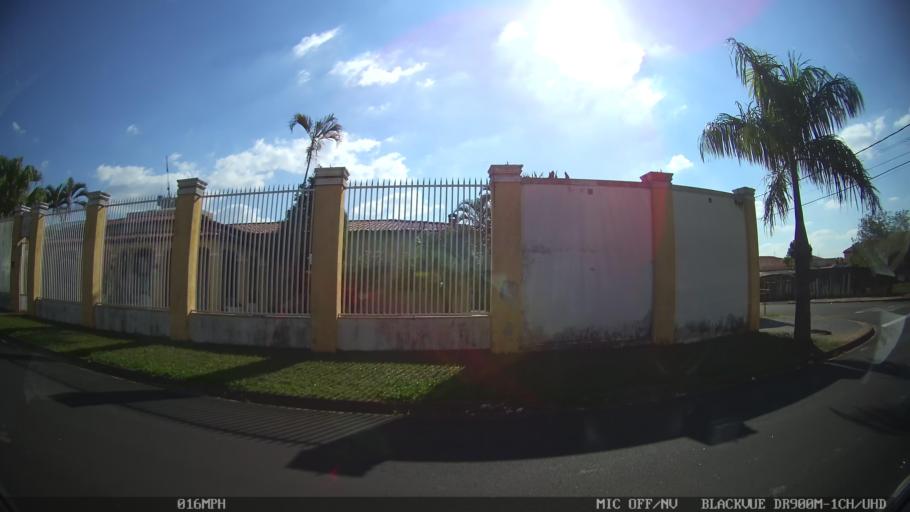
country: BR
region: Sao Paulo
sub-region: Sumare
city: Sumare
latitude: -22.8130
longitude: -47.2855
